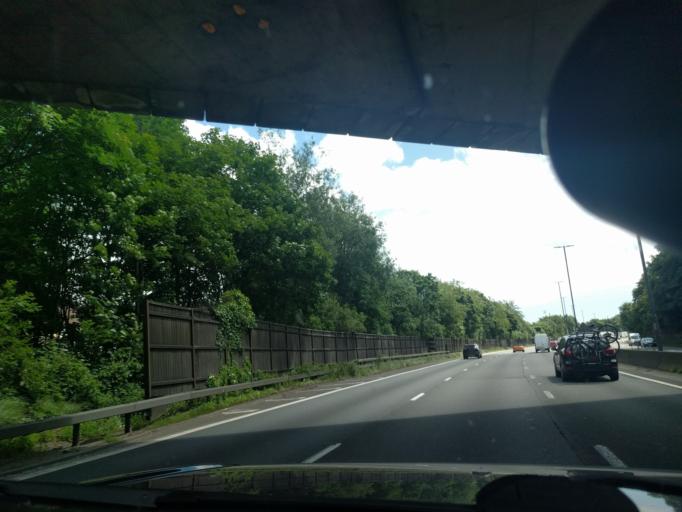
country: GB
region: Wales
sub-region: Newport
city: Caerleon
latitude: 51.6006
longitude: -2.9710
